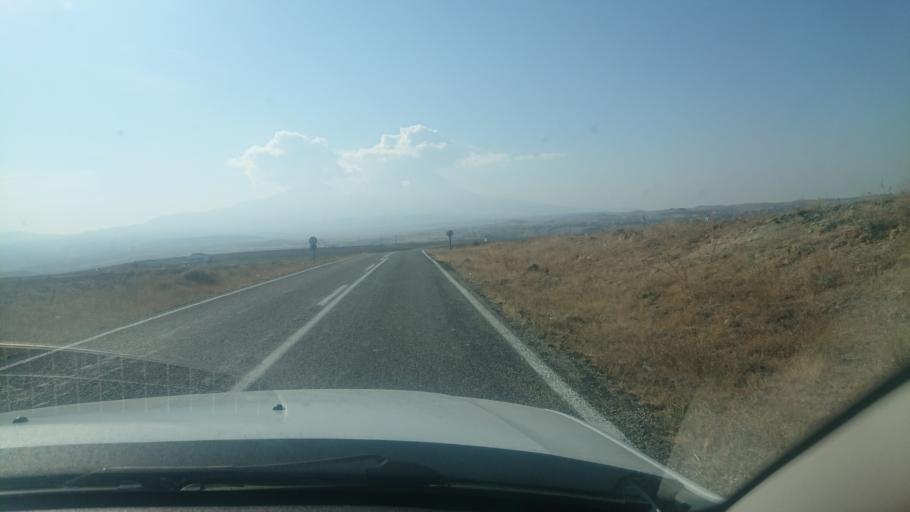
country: TR
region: Aksaray
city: Guzelyurt
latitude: 38.2487
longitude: 34.3270
